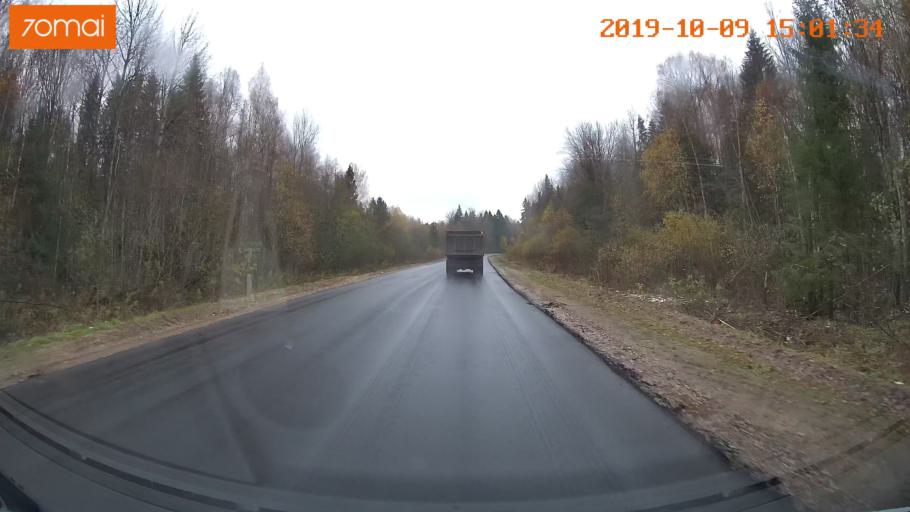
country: RU
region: Kostroma
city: Chistyye Bory
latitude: 58.2952
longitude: 41.6809
